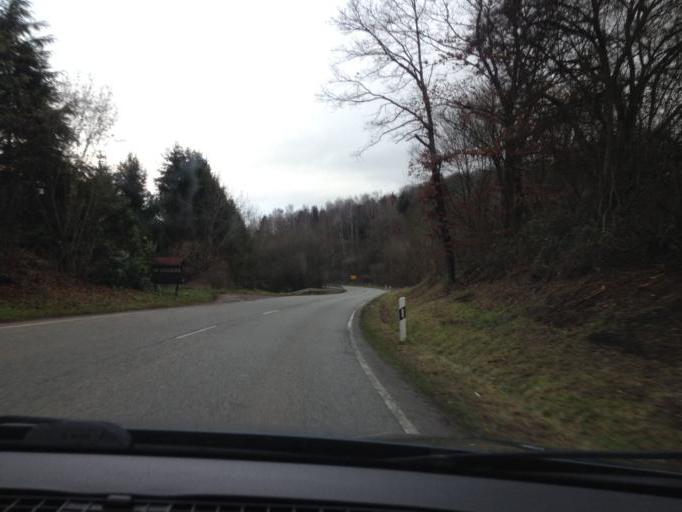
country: DE
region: Rheinland-Pfalz
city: Breitenbach
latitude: 49.4264
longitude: 7.2364
